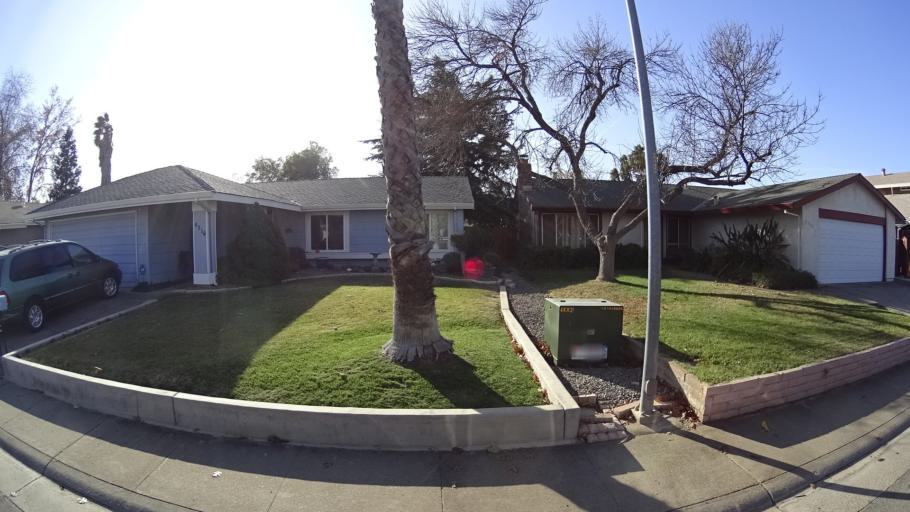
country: US
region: California
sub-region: Sacramento County
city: Antelope
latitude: 38.6984
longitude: -121.3127
